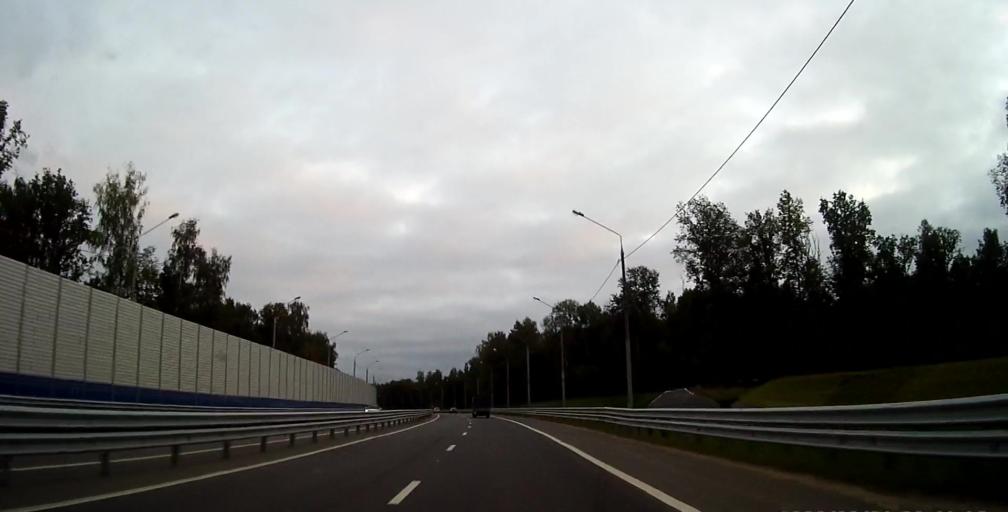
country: RU
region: Moskovskaya
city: Dubrovitsy
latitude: 55.4035
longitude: 37.5003
